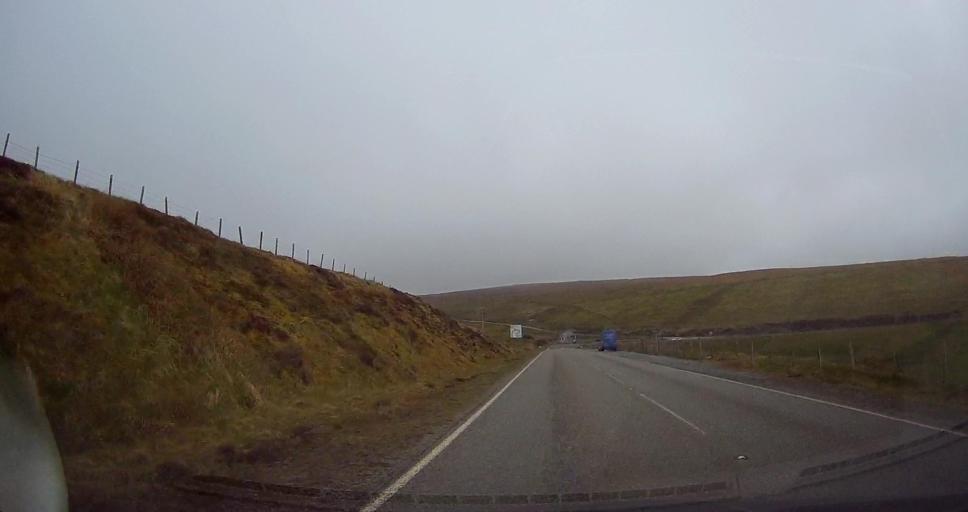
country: GB
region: Scotland
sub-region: Shetland Islands
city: Sandwick
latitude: 59.9864
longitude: -1.2810
